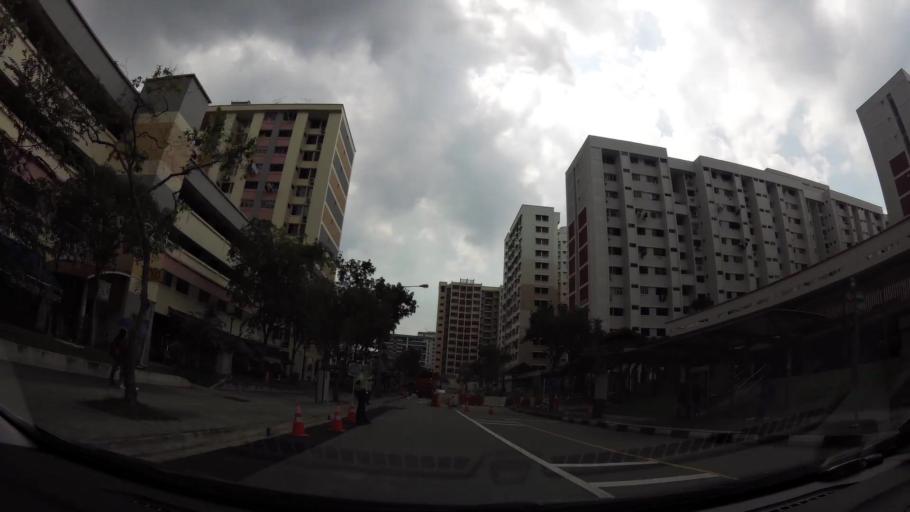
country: SG
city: Singapore
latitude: 1.3513
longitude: 103.9337
